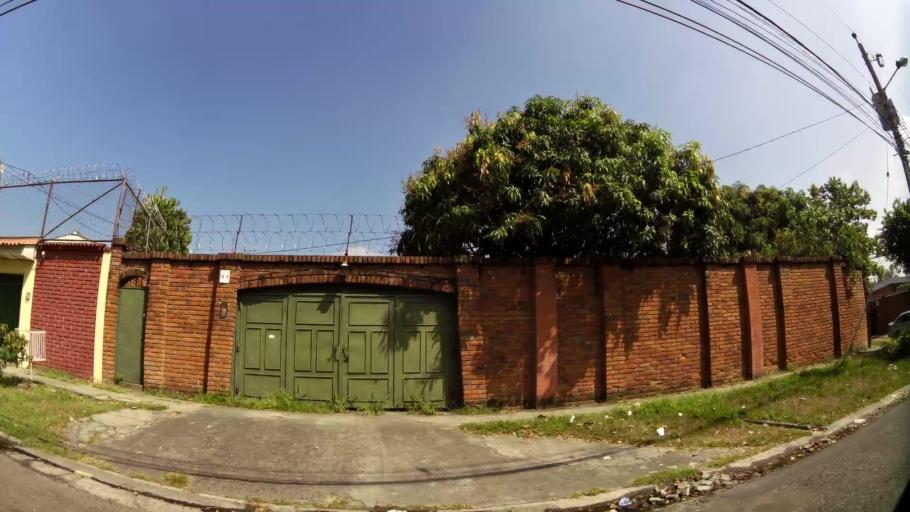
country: SV
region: La Libertad
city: Antiguo Cuscatlan
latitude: 13.6856
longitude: -89.2261
